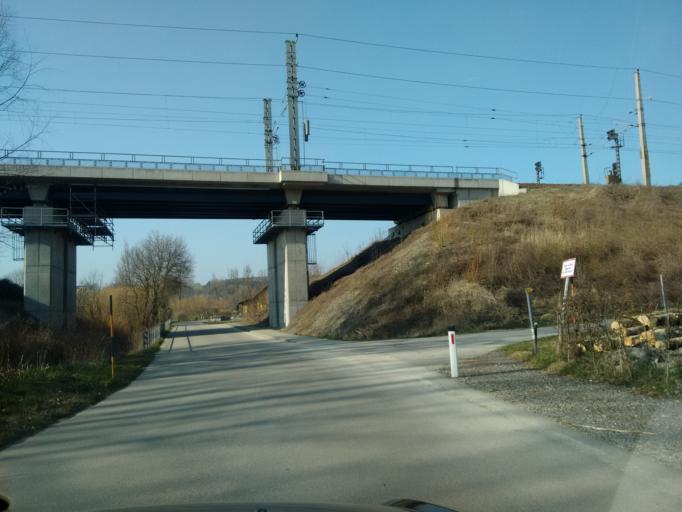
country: AT
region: Upper Austria
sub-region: Politischer Bezirk Grieskirchen
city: Bad Schallerbach
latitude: 48.2147
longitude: 13.9571
